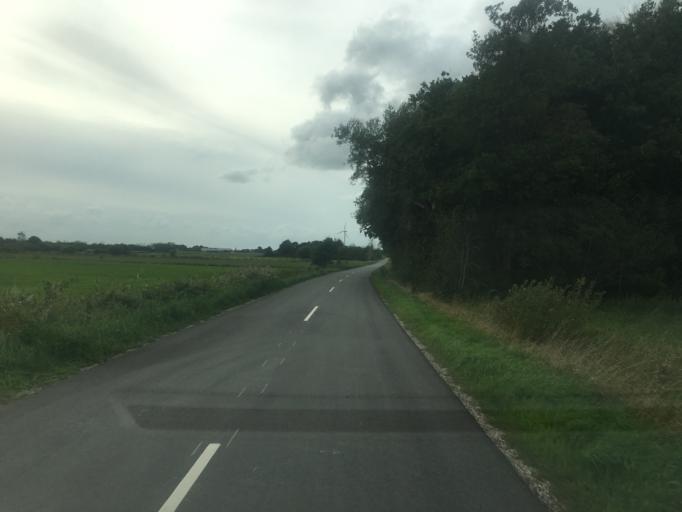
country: DE
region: Schleswig-Holstein
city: Aventoft
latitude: 54.9653
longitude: 8.7904
